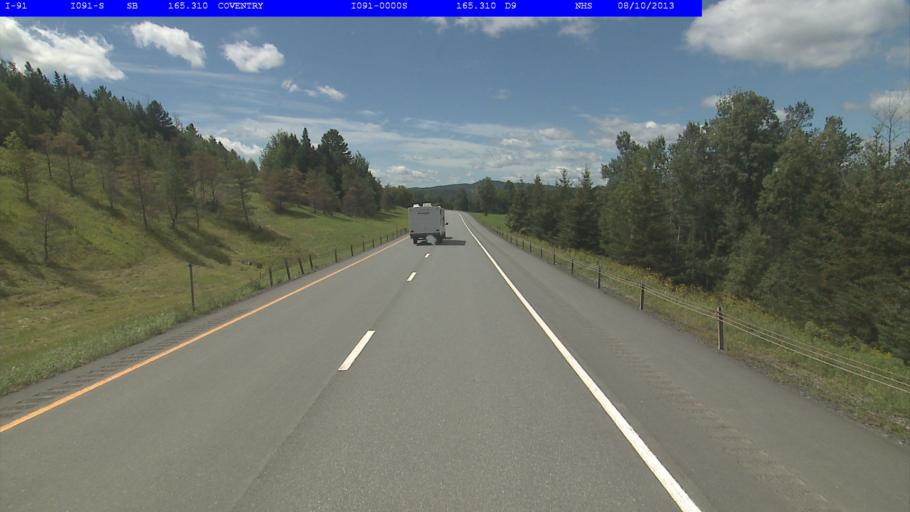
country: US
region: Vermont
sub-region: Orleans County
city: Newport
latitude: 44.8590
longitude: -72.1909
